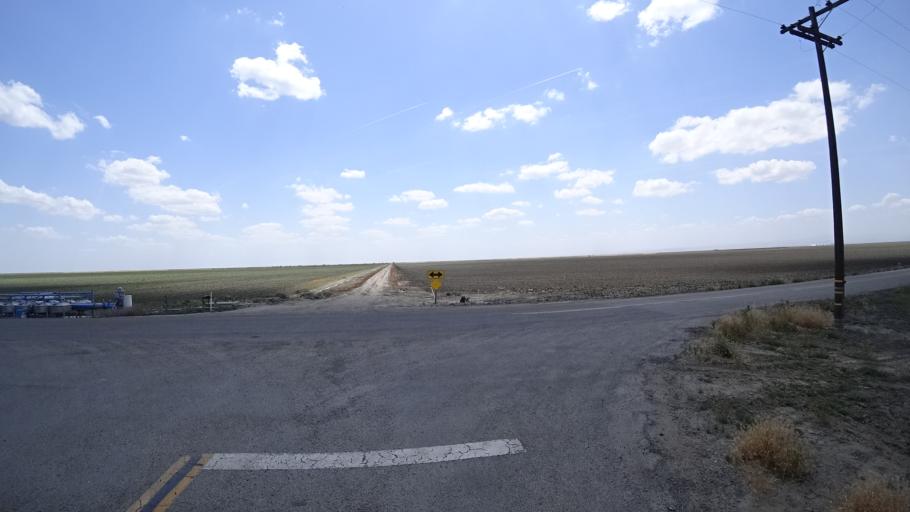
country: US
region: California
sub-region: Kings County
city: Stratford
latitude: 36.1527
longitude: -119.8160
